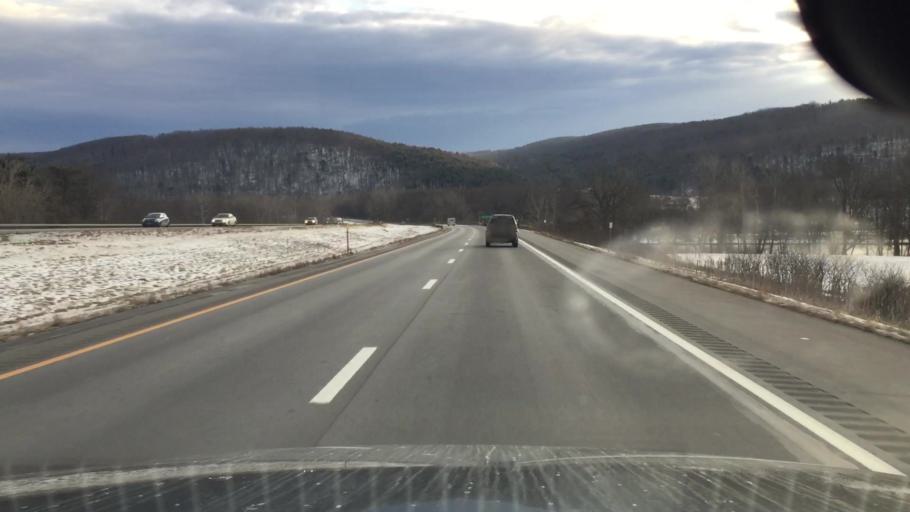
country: US
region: Pennsylvania
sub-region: Bradford County
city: Sayre
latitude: 42.0066
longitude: -76.4728
